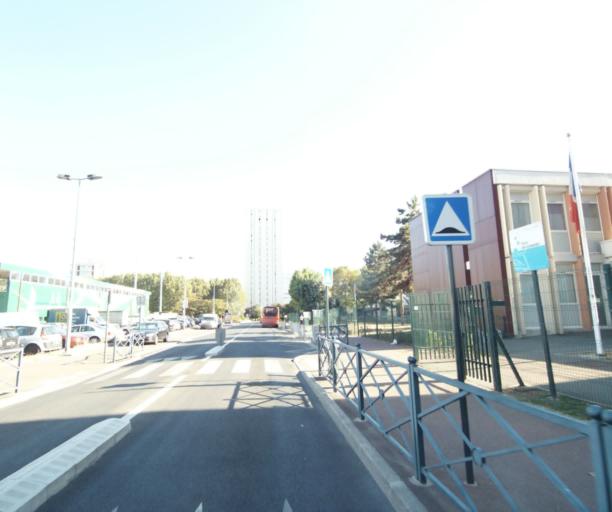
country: FR
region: Ile-de-France
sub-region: Departement des Hauts-de-Seine
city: Villeneuve-la-Garenne
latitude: 48.9394
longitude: 2.3278
